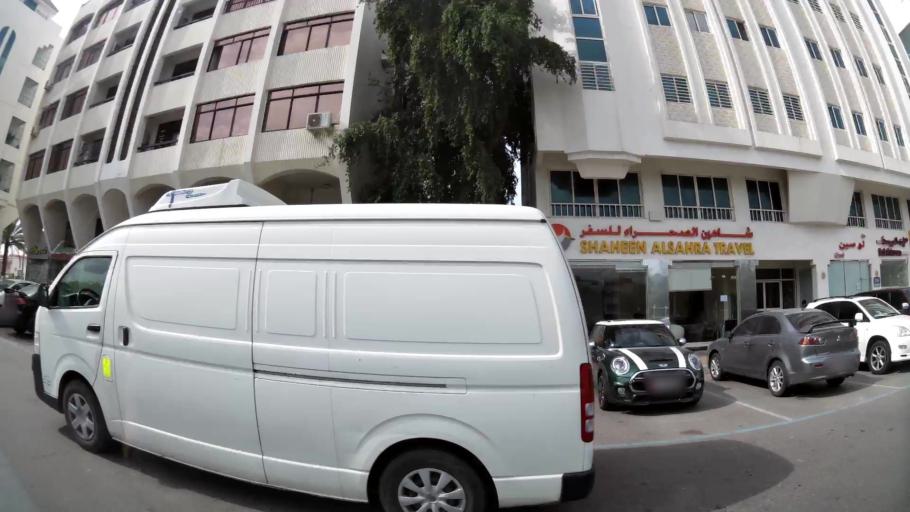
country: AE
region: Abu Dhabi
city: Abu Dhabi
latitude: 24.4553
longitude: 54.3839
